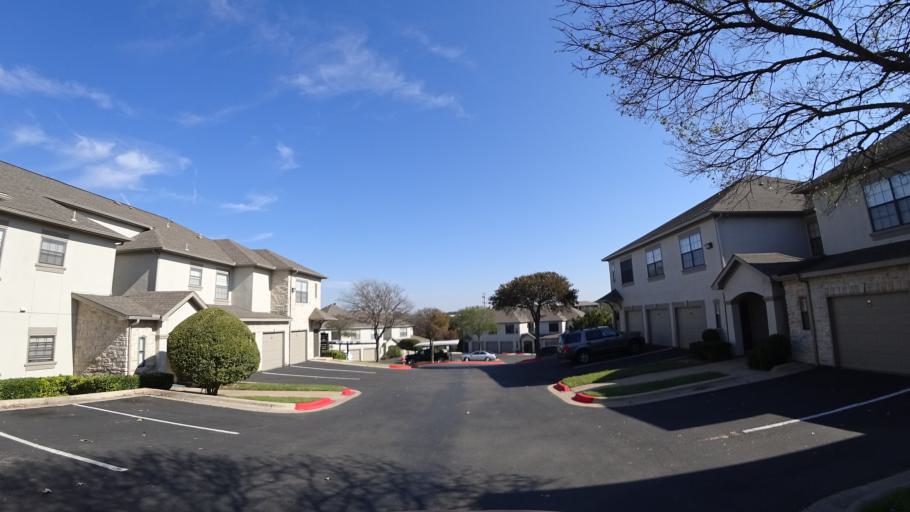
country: US
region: Texas
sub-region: Williamson County
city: Jollyville
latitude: 30.3784
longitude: -97.7696
